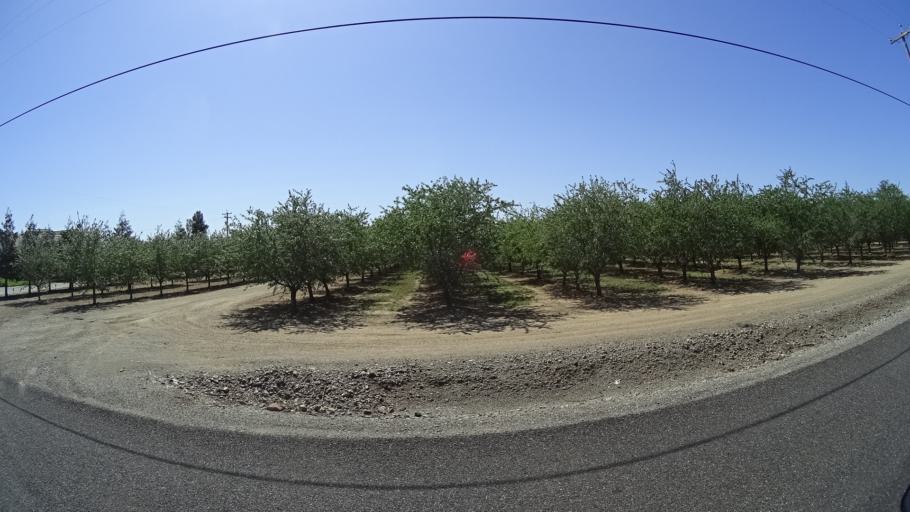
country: US
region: California
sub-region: Glenn County
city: Hamilton City
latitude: 39.7897
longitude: -122.0904
